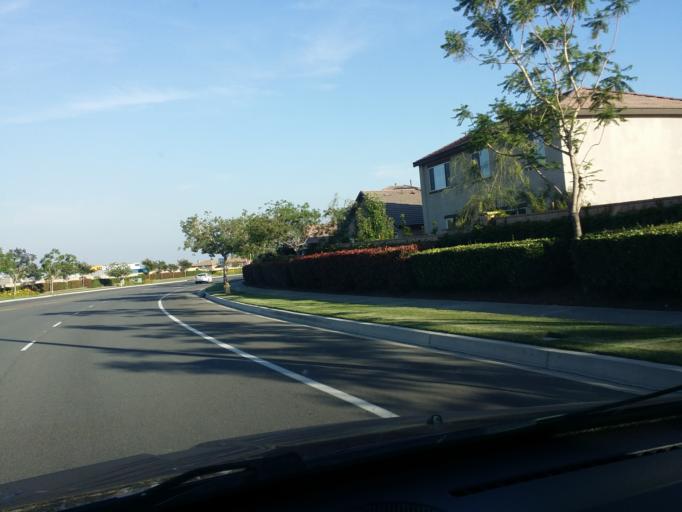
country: US
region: California
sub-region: San Bernardino County
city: Muscoy
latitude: 34.1874
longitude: -117.4107
